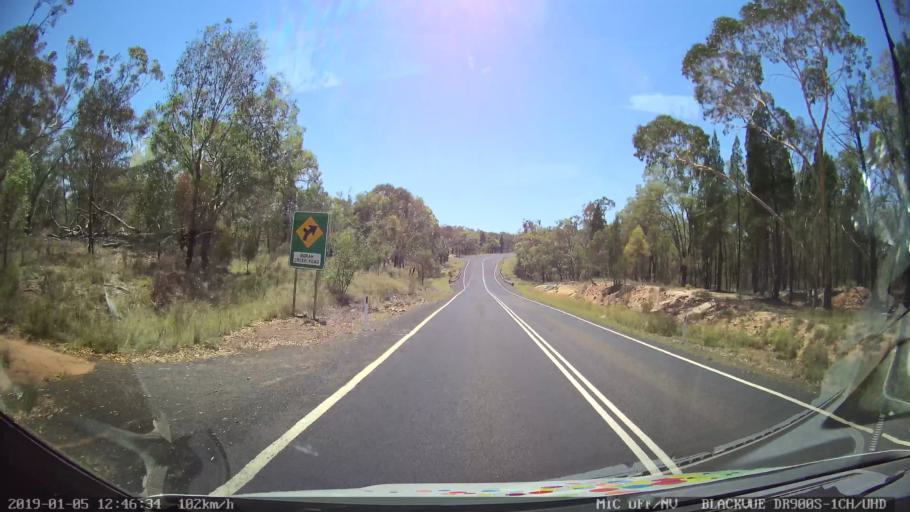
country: AU
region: New South Wales
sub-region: Warrumbungle Shire
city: Coonabarabran
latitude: -31.1167
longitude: 149.5642
